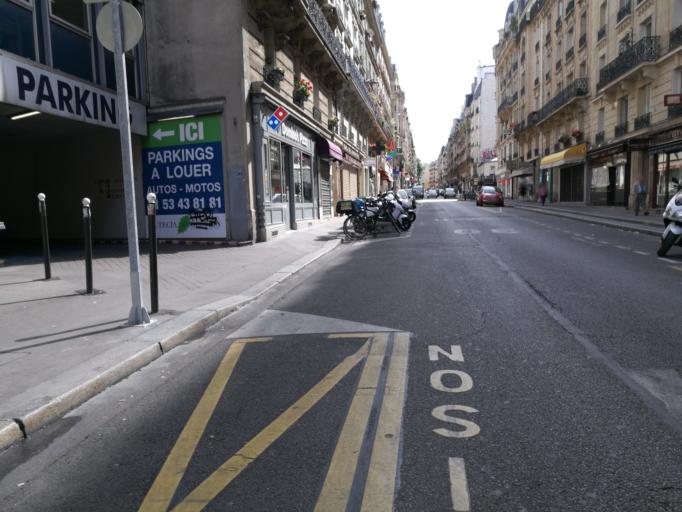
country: FR
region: Ile-de-France
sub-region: Paris
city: Saint-Ouen
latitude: 48.8913
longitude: 2.3347
